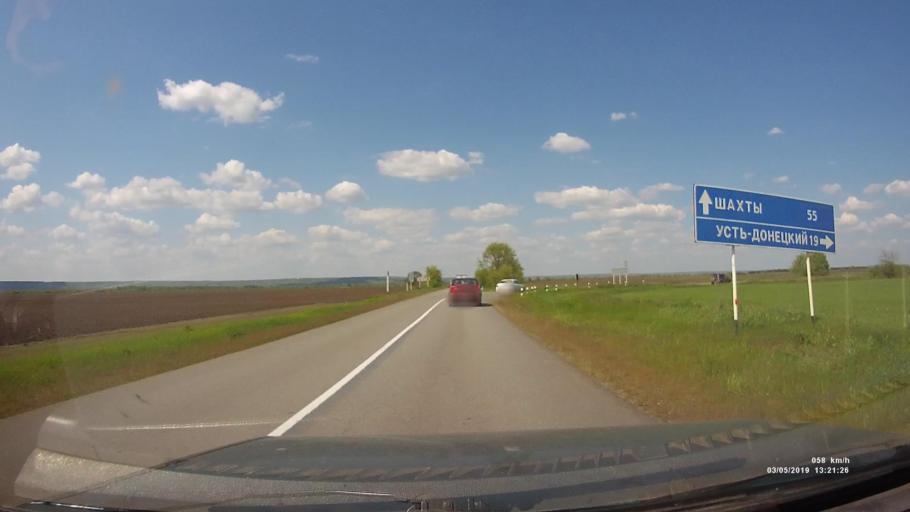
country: RU
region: Rostov
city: Semikarakorsk
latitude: 47.5548
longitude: 40.7472
